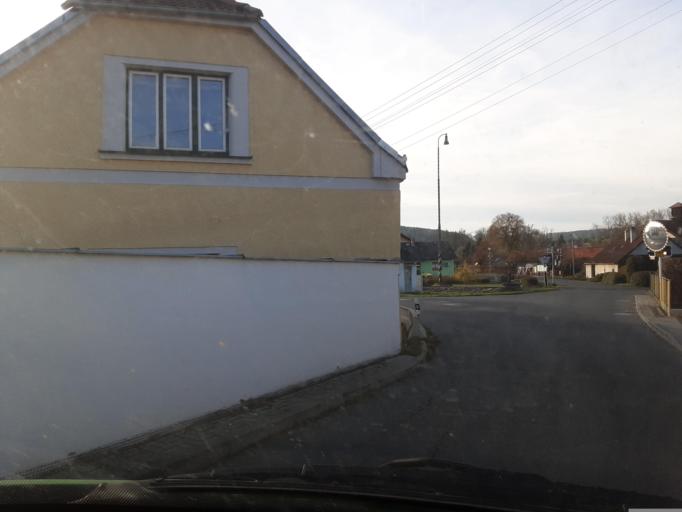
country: CZ
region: Plzensky
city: Horazd'ovice
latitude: 49.2977
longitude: 13.6670
